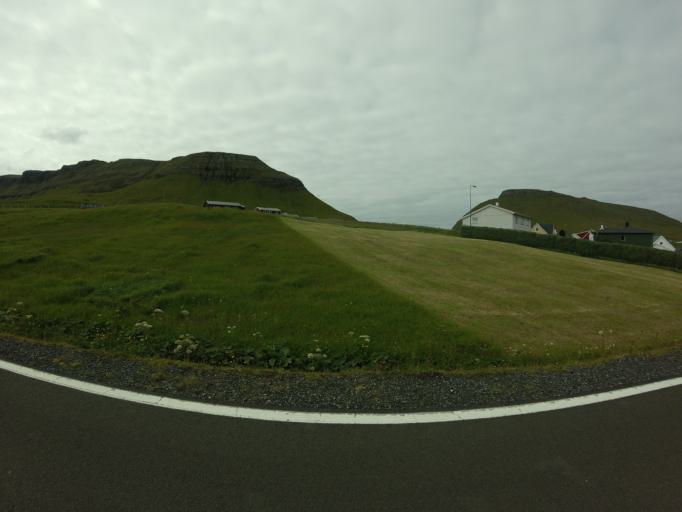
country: FO
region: Suduroy
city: Tvoroyri
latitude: 61.5973
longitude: -6.9477
